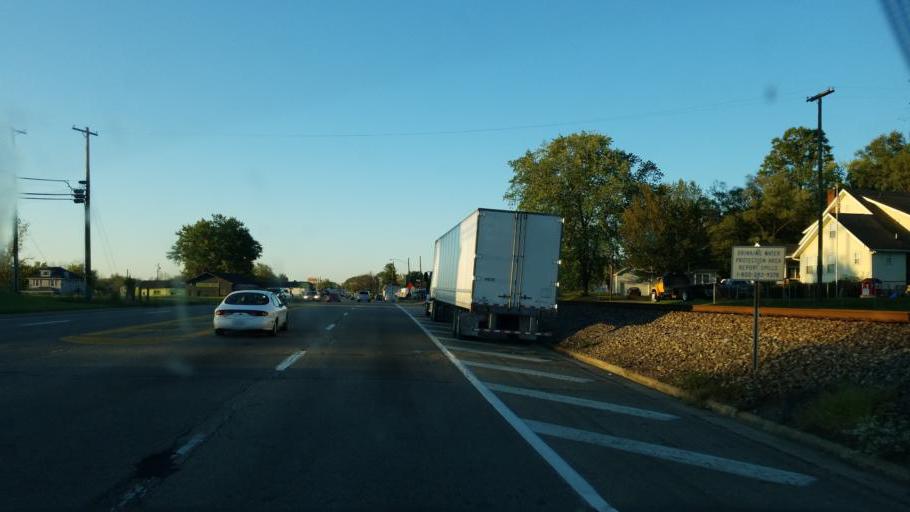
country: US
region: Ohio
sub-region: Scioto County
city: Lucasville
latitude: 38.8731
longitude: -82.9953
